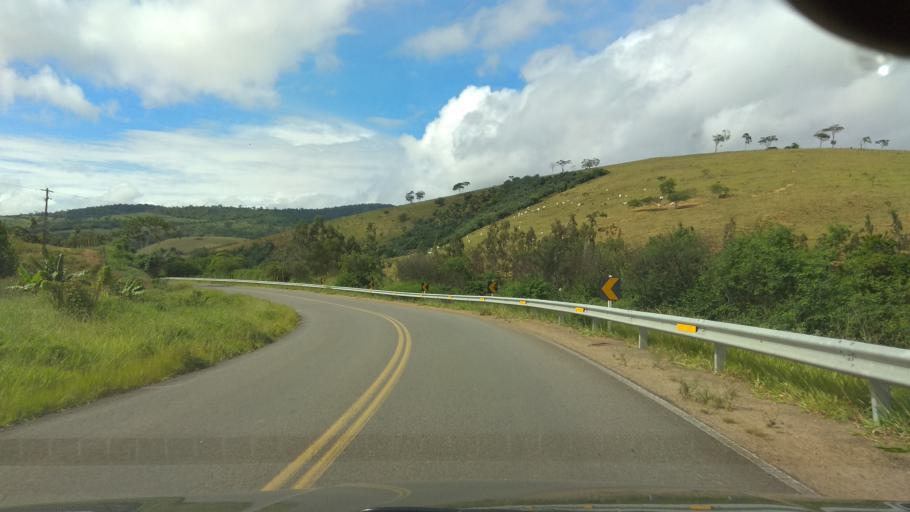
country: BR
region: Bahia
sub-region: Ubaira
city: Ubaira
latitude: -13.2621
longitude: -39.7008
